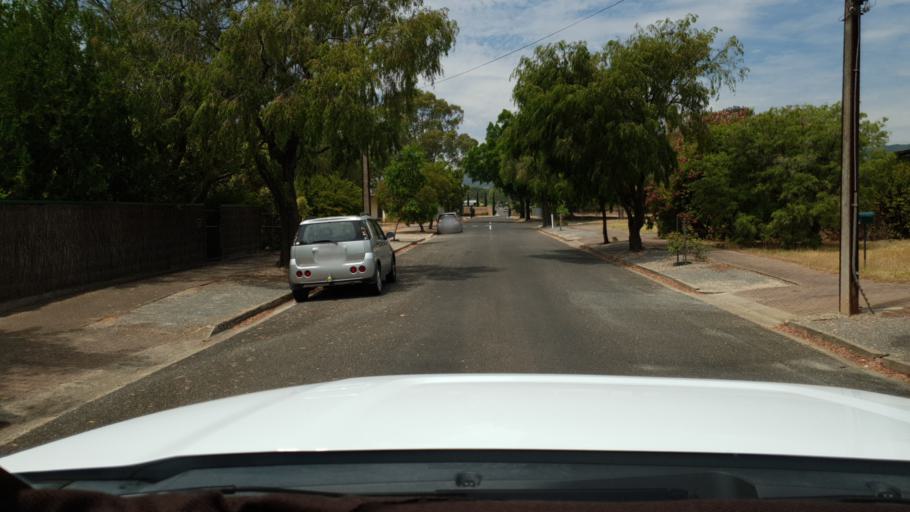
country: AU
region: South Australia
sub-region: Marion
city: Clovelly Park
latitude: -34.9979
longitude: 138.5828
